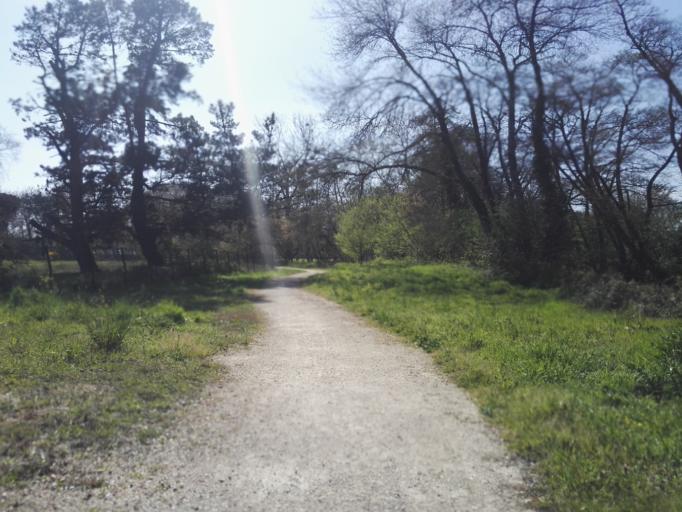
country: FR
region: Aquitaine
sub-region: Departement de la Gironde
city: Gradignan
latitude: 44.7769
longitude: -0.5893
